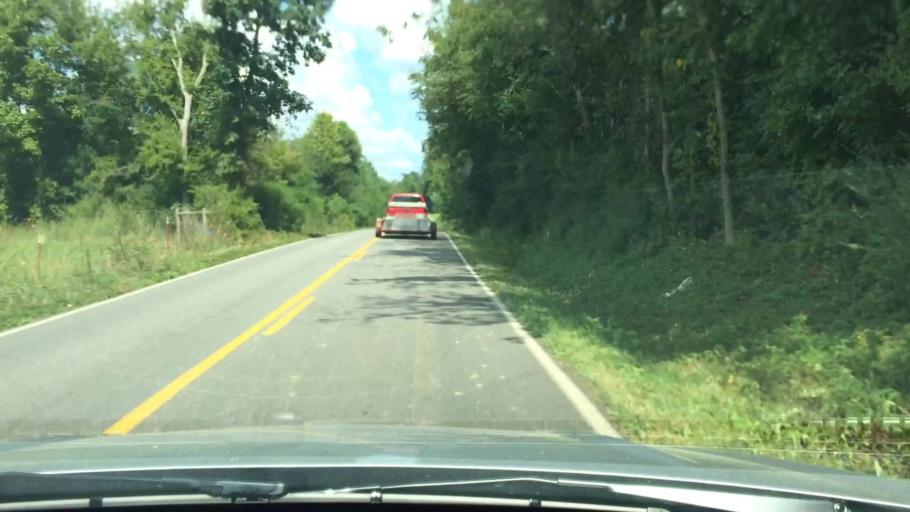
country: US
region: Tennessee
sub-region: Monroe County
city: Sweetwater
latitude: 35.5298
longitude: -84.4587
